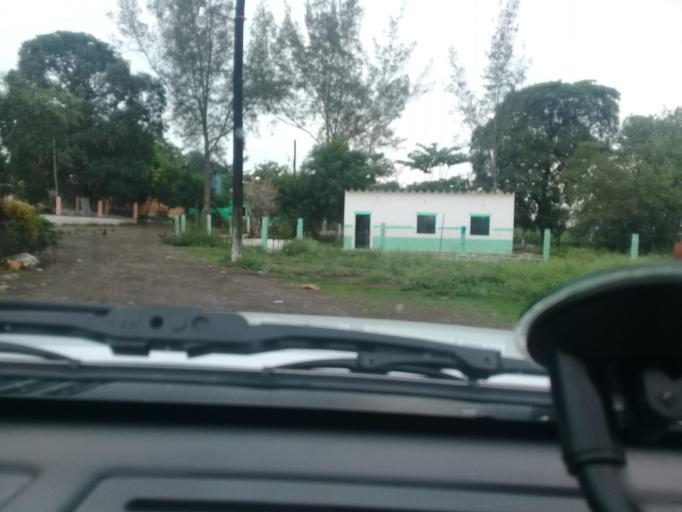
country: MX
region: Veracruz
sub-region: Puente Nacional
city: Chichicaxtle
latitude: 19.3681
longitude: -96.4330
